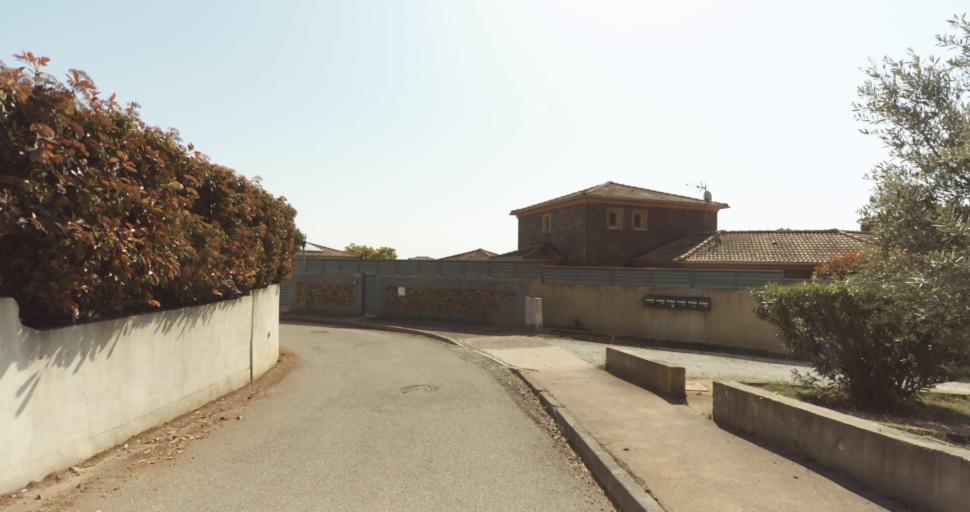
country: FR
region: Corsica
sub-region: Departement de la Haute-Corse
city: Biguglia
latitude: 42.6248
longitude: 9.4251
